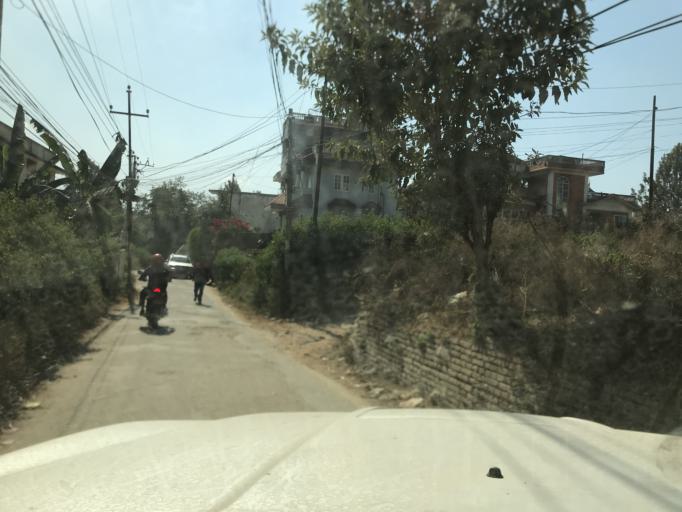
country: NP
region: Central Region
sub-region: Bagmati Zone
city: Patan
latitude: 27.6490
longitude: 85.3159
